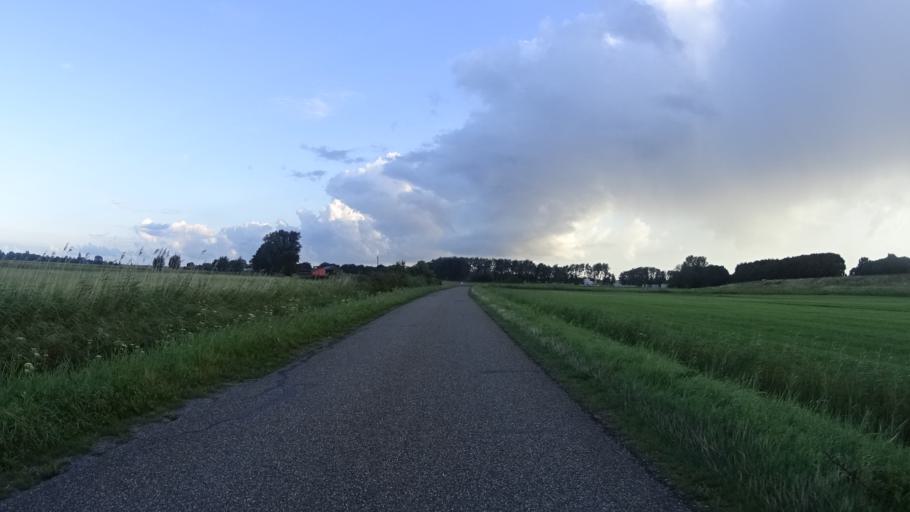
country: NL
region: North Holland
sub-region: Gemeente Hollands Kroon
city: Den Oever
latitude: 52.9244
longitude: 5.0330
